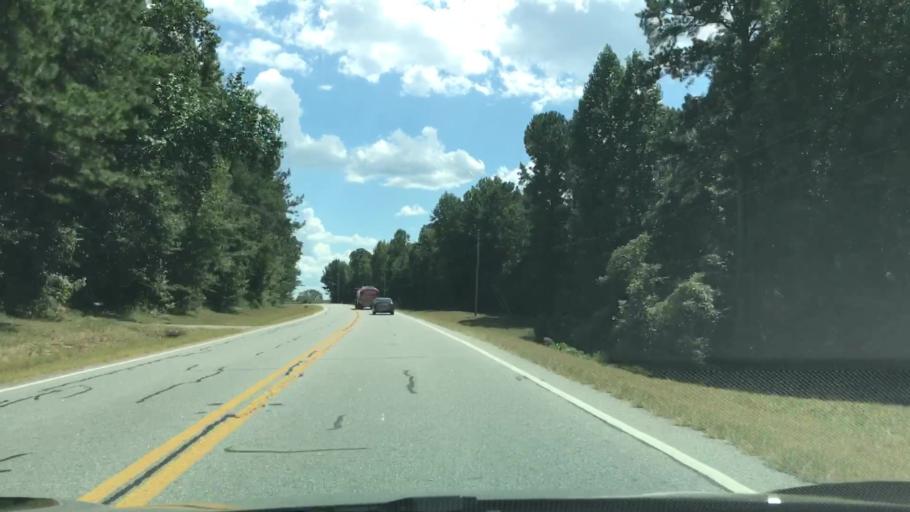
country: US
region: Georgia
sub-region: Oconee County
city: Watkinsville
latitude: 33.7620
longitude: -83.3089
